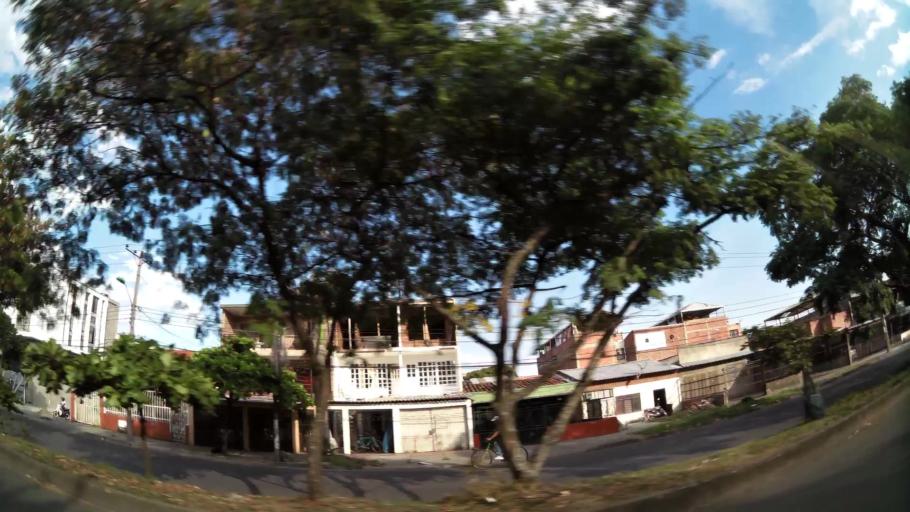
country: CO
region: Valle del Cauca
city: Cali
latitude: 3.4395
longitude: -76.4928
